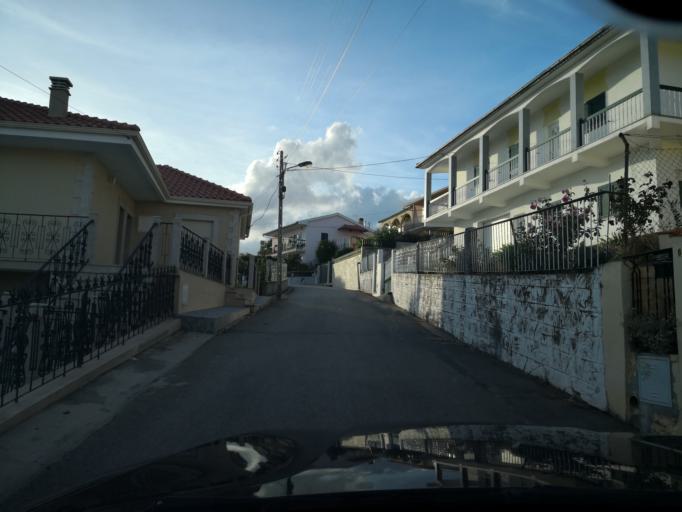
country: PT
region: Vila Real
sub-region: Santa Marta de Penaguiao
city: Santa Marta de Penaguiao
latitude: 41.2317
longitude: -7.8110
